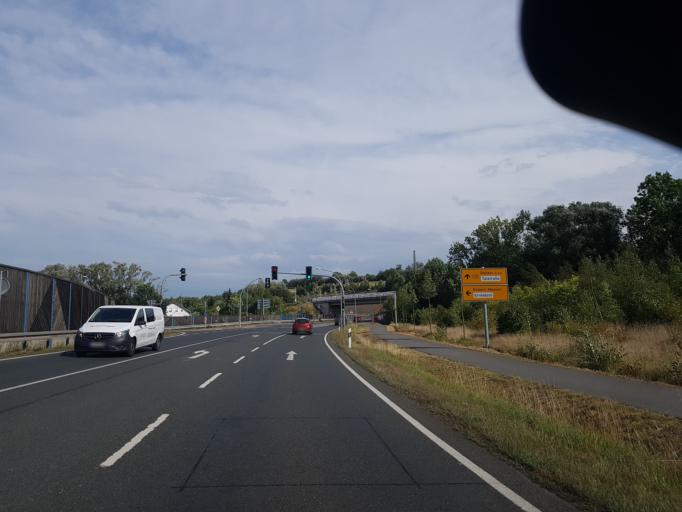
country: DE
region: Saxony
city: Dobeln
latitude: 51.1249
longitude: 13.0666
